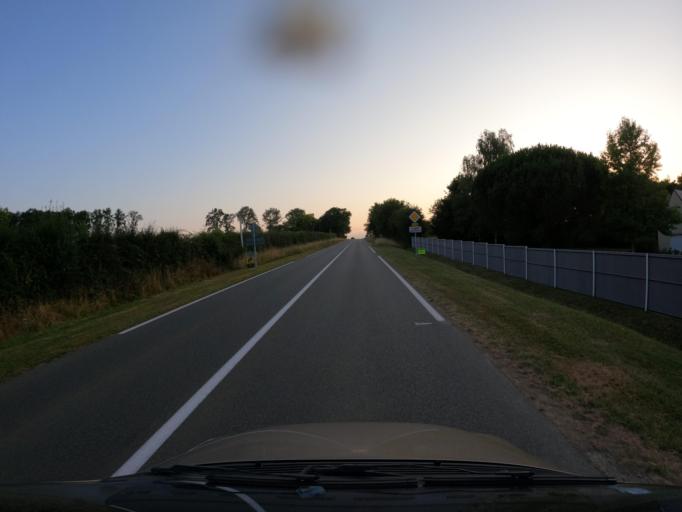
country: FR
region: Pays de la Loire
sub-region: Departement de la Mayenne
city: Aze
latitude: 47.8520
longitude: -0.6153
